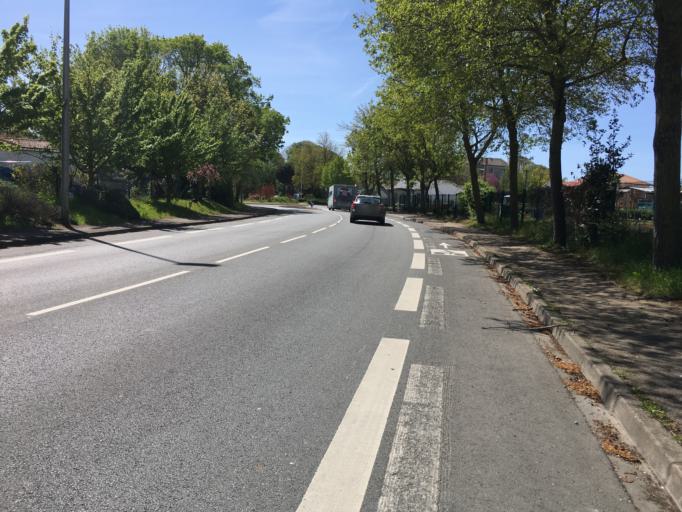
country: FR
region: Poitou-Charentes
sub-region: Departement de la Charente-Maritime
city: La Rochelle
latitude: 46.1405
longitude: -1.1442
